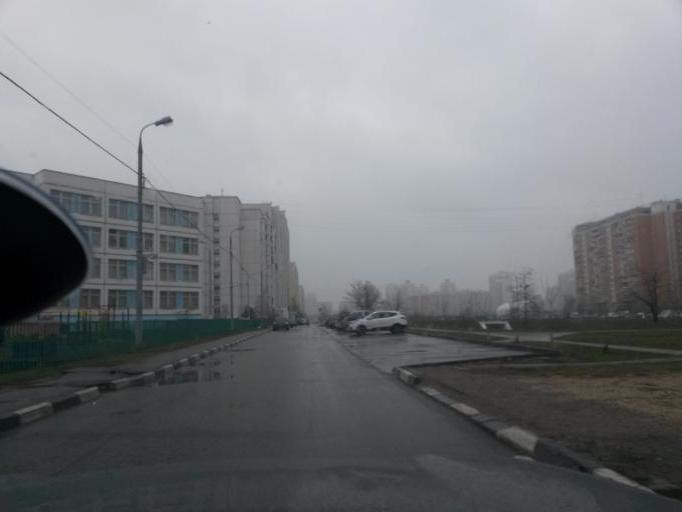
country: RU
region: Moscow
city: Brateyevo
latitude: 55.6556
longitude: 37.7709
